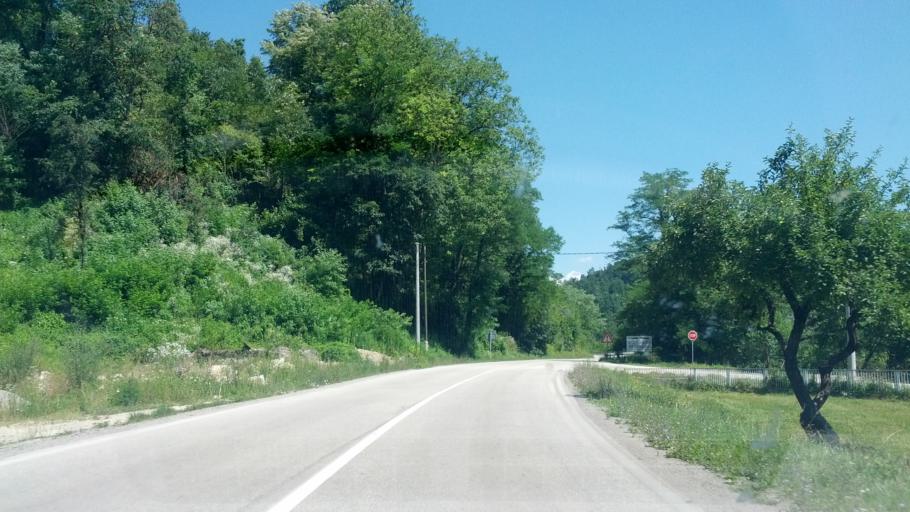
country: BA
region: Federation of Bosnia and Herzegovina
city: Bosanska Krupa
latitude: 44.9201
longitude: 16.1458
